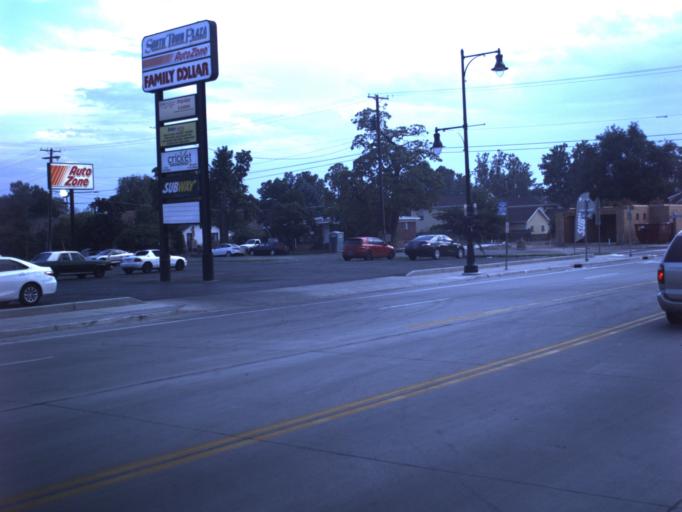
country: US
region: Utah
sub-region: Utah County
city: Provo
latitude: 40.2297
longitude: -111.6476
